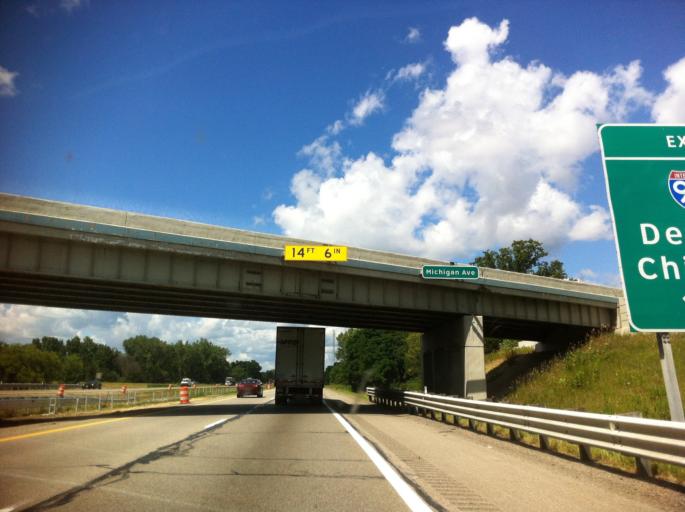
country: US
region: Michigan
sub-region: Washtenaw County
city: Ypsilanti
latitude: 42.2057
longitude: -83.6848
